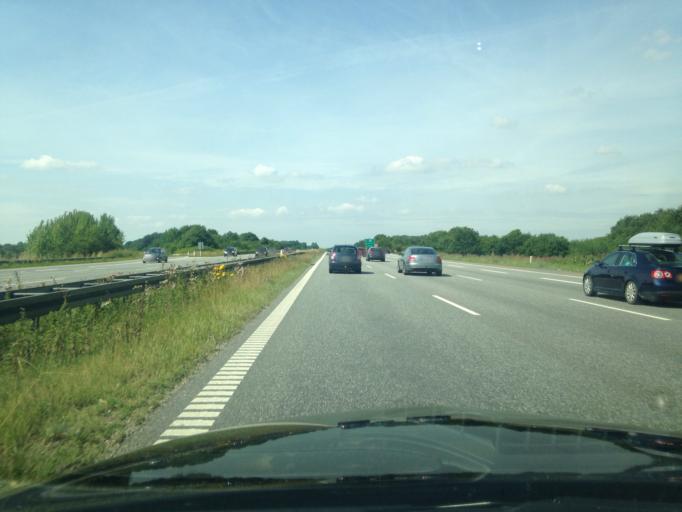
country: DK
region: South Denmark
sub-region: Fredericia Kommune
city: Snoghoj
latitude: 55.5366
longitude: 9.6961
